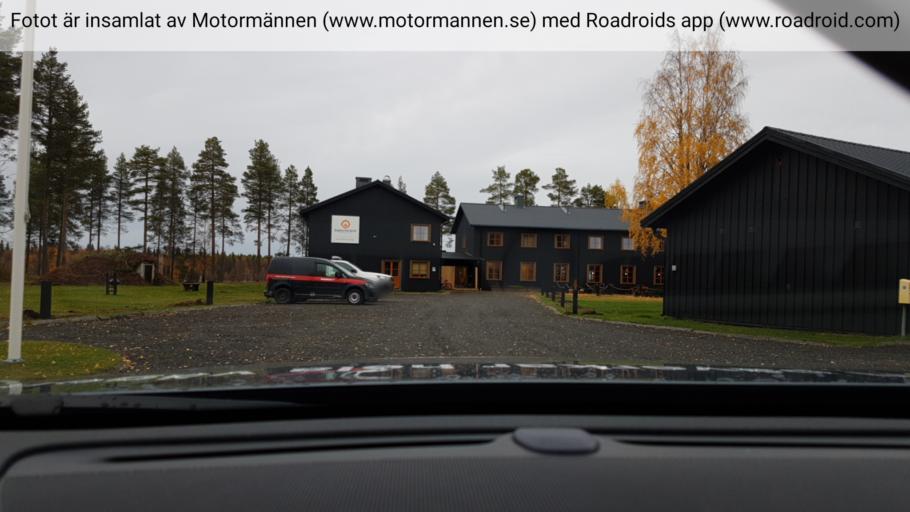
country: SE
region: Norrbotten
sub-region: Pajala Kommun
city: Pajala
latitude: 67.1771
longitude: 22.6663
